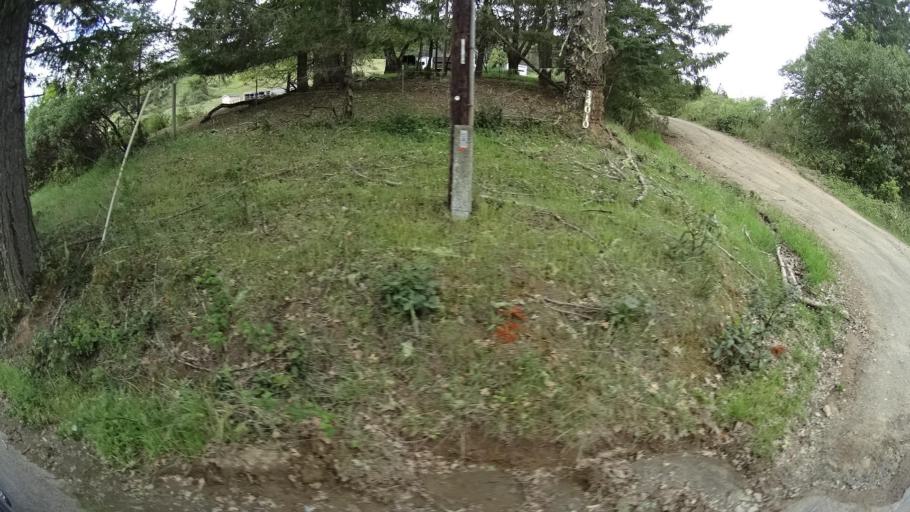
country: US
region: California
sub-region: Humboldt County
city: Redway
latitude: 40.1342
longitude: -123.6281
